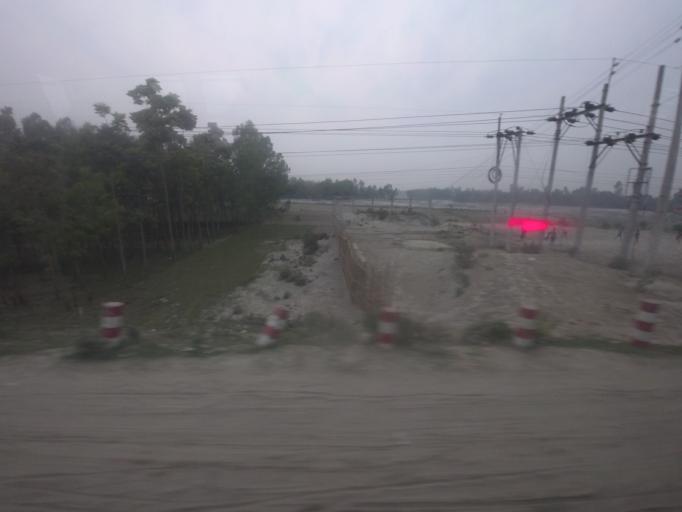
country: BD
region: Dhaka
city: Tangail
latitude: 24.3145
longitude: 89.9230
